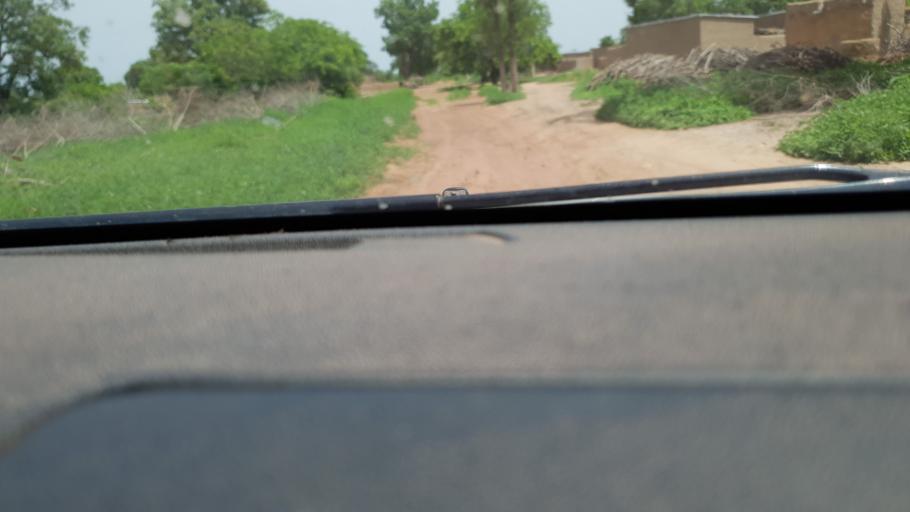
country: ML
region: Koulikoro
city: Koulikoro
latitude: 12.6700
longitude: -7.2466
